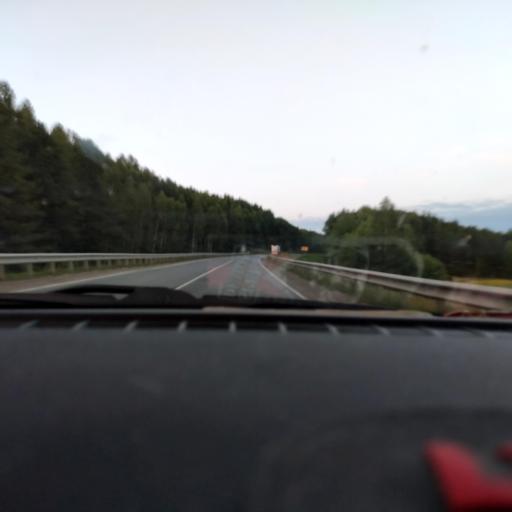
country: RU
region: Perm
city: Nytva
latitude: 57.9899
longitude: 55.2384
